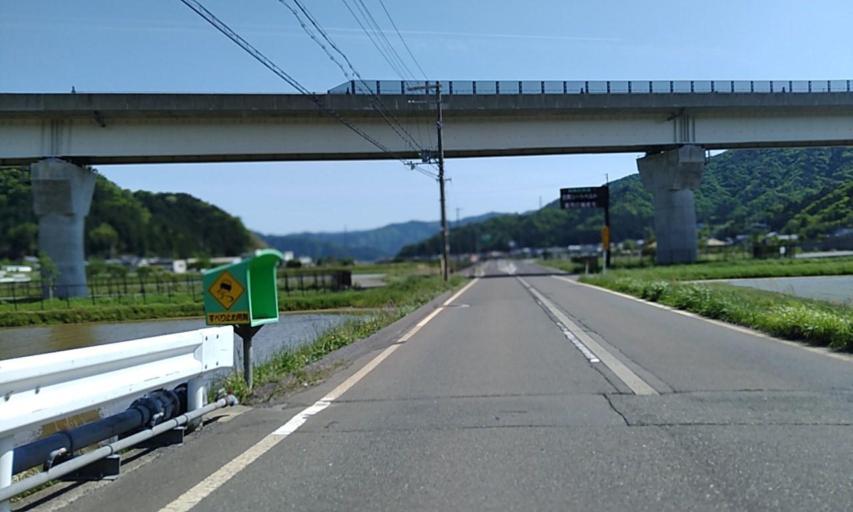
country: JP
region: Fukui
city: Obama
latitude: 35.5119
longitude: 135.8686
